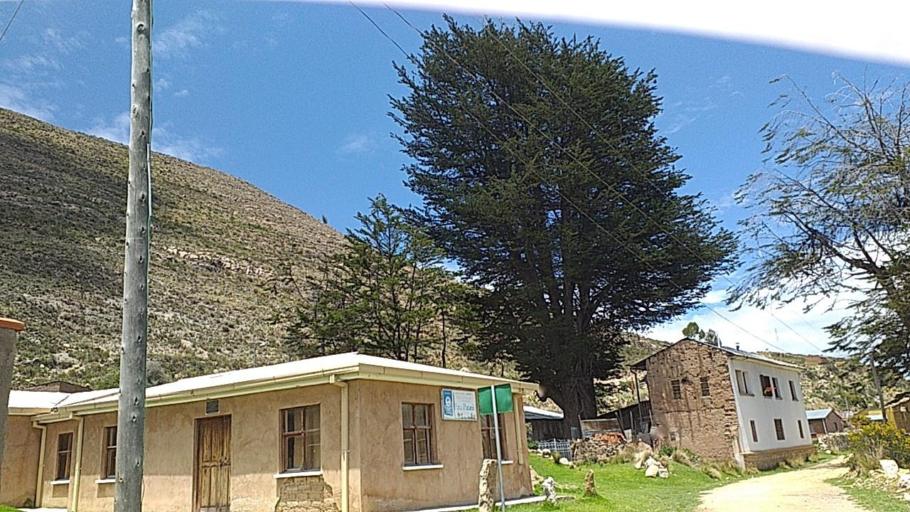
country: BO
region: La Paz
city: Huatajata
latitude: -16.3120
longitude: -68.6777
